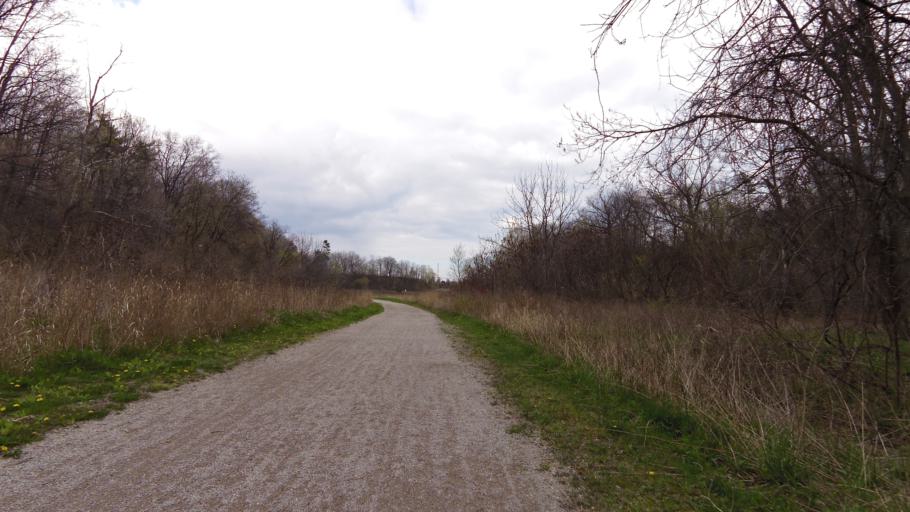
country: CA
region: Ontario
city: Etobicoke
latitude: 43.6472
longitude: -79.6129
